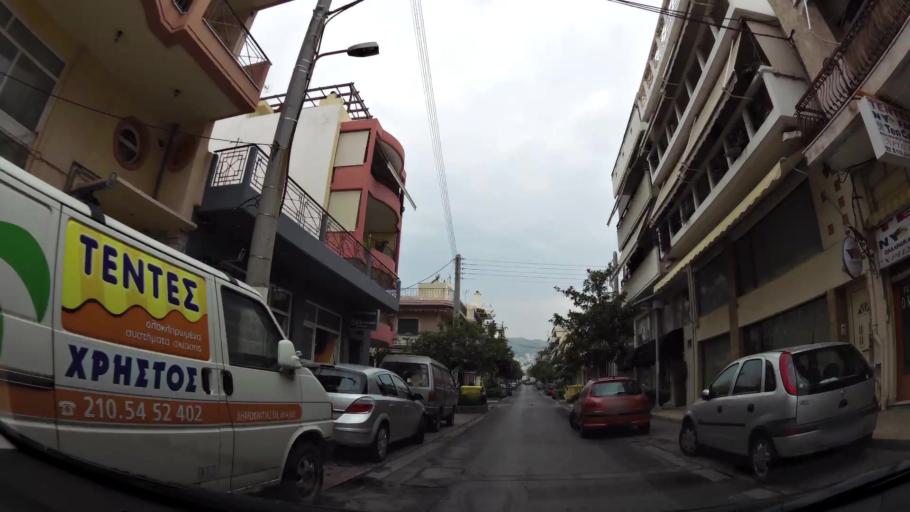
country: GR
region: Attica
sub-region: Nomarchia Athinas
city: Agia Varvara
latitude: 37.9875
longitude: 23.6694
